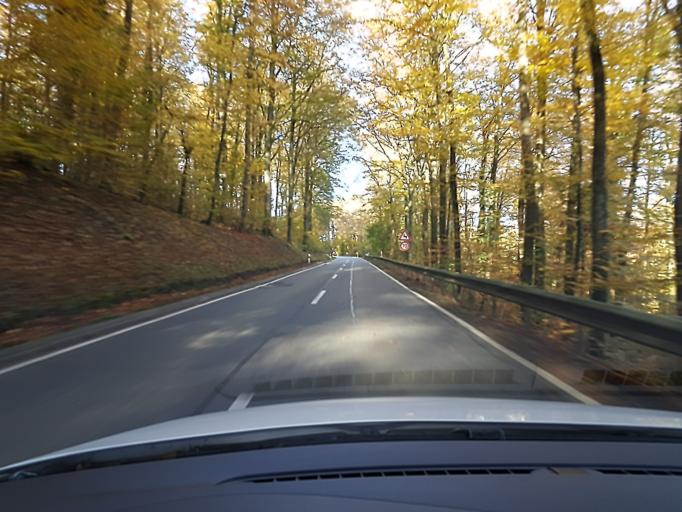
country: DE
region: Baden-Wuerttemberg
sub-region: Karlsruhe Region
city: Fahrenbach
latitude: 49.3968
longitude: 9.1895
